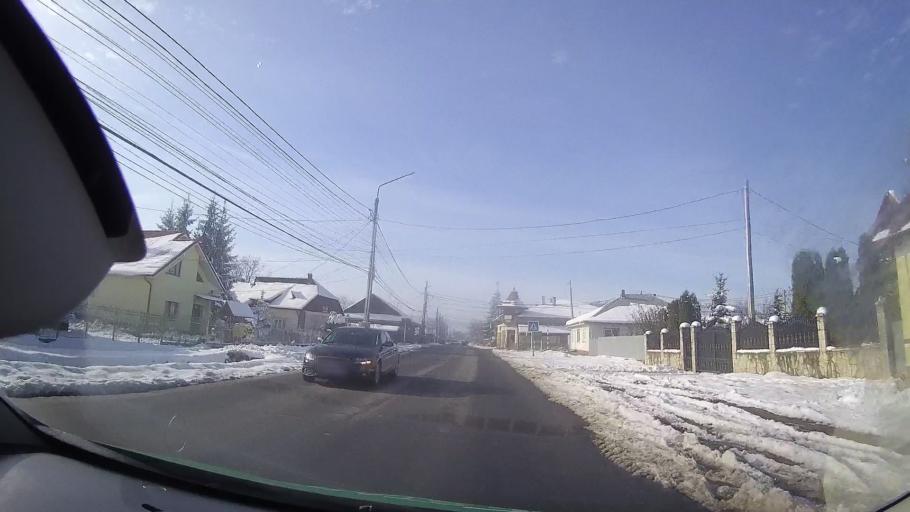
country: RO
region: Neamt
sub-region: Oras Targu Neamt
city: Targu Neamt
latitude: 47.2086
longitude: 26.3867
